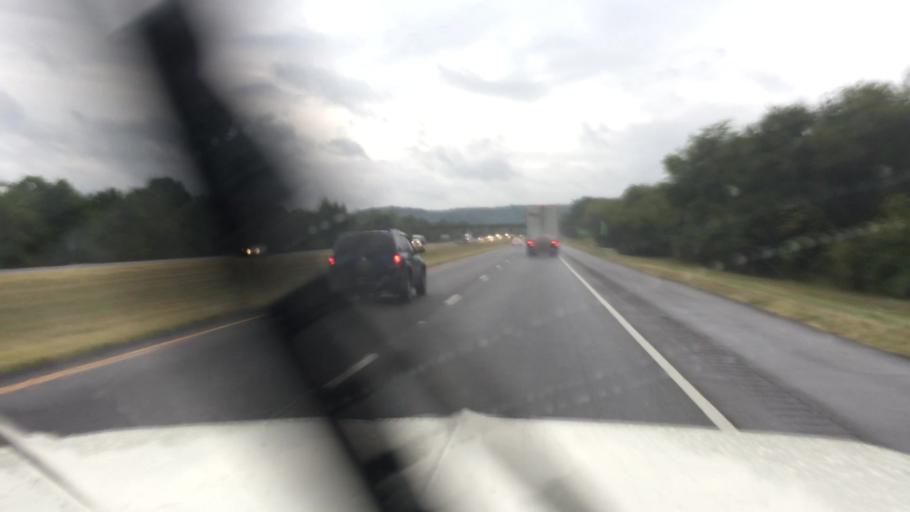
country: US
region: Alabama
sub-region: Morgan County
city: Falkville
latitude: 34.3567
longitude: -86.8919
